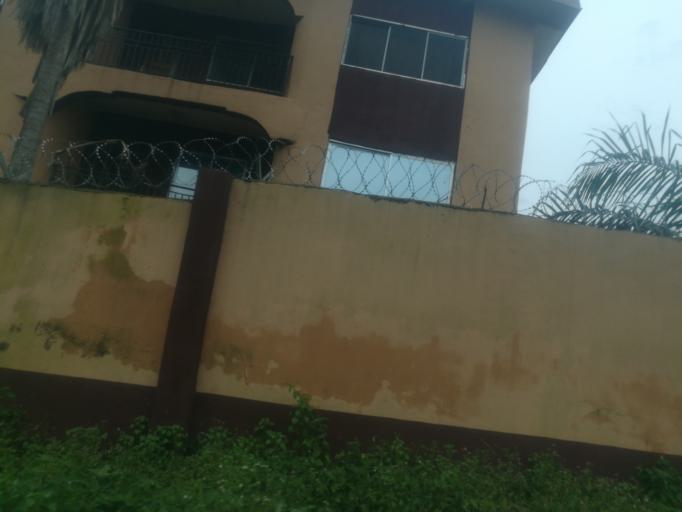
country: NG
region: Oyo
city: Egbeda
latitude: 7.3869
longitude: 3.9850
